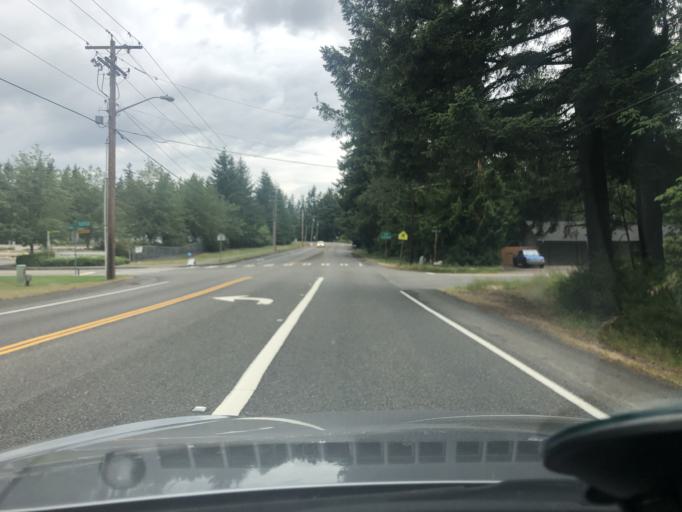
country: US
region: Washington
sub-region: King County
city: Black Diamond
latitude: 47.3220
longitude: -122.0387
